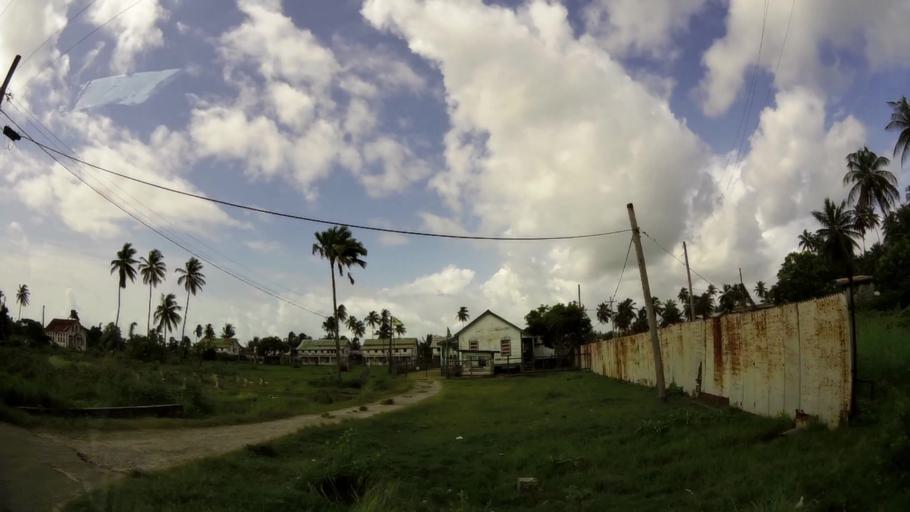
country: GY
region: Demerara-Mahaica
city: Mahaica Village
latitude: 6.7107
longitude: -57.9269
